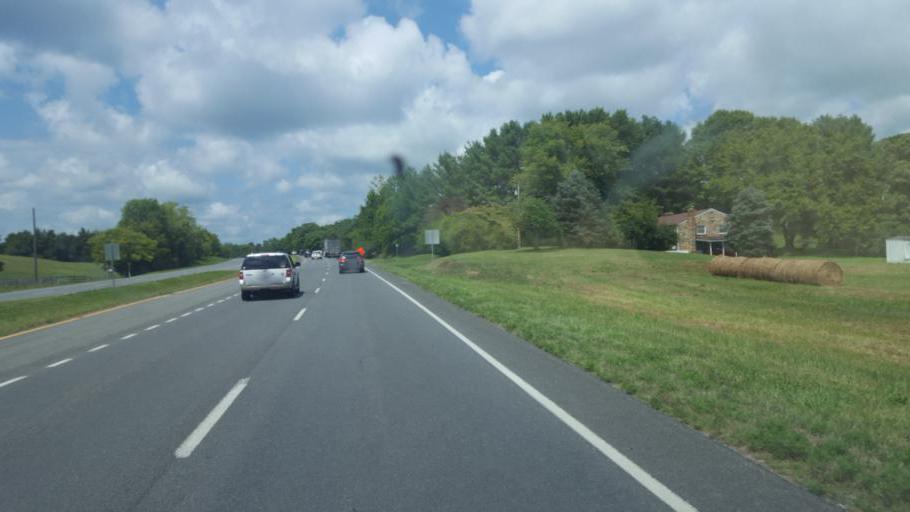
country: US
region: Virginia
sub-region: Fauquier County
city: Bealeton
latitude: 38.5981
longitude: -77.7743
